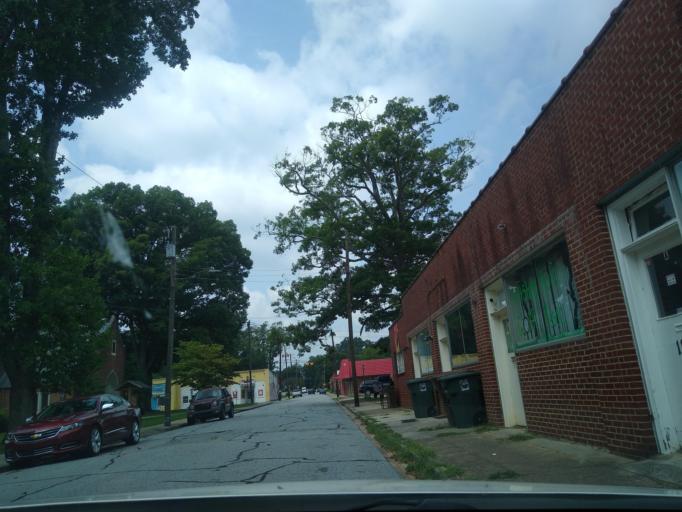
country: US
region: North Carolina
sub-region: Guilford County
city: Greensboro
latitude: 36.0533
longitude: -79.8102
